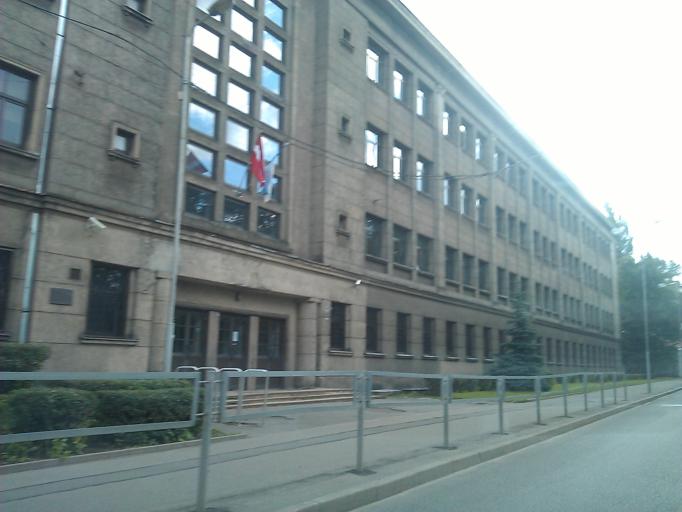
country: LV
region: Riga
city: Riga
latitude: 56.9584
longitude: 24.1406
